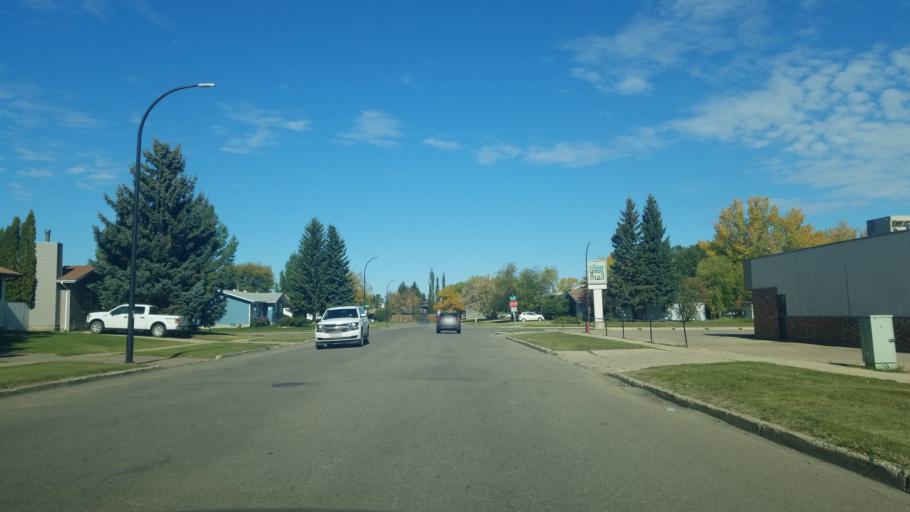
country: CA
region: Saskatchewan
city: Lloydminster
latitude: 53.2726
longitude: -110.0121
